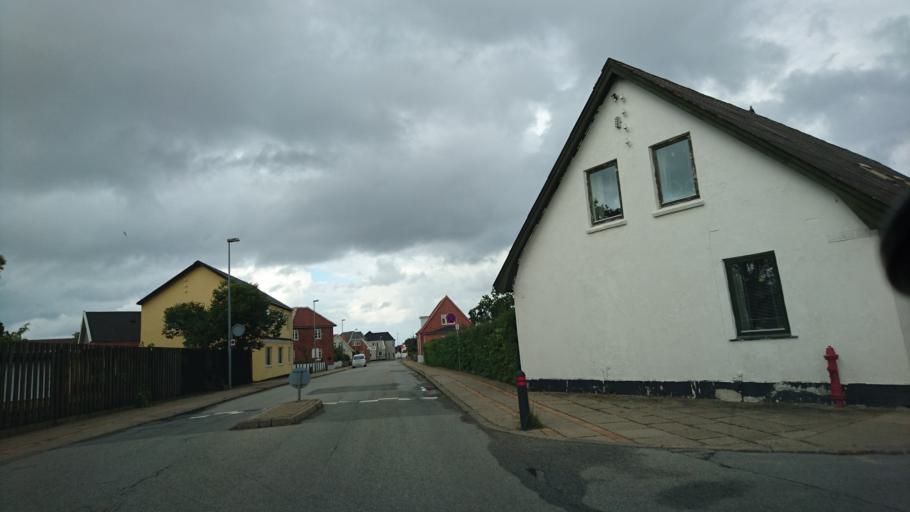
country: DK
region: North Denmark
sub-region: Frederikshavn Kommune
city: Frederikshavn
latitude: 57.4253
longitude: 10.5171
